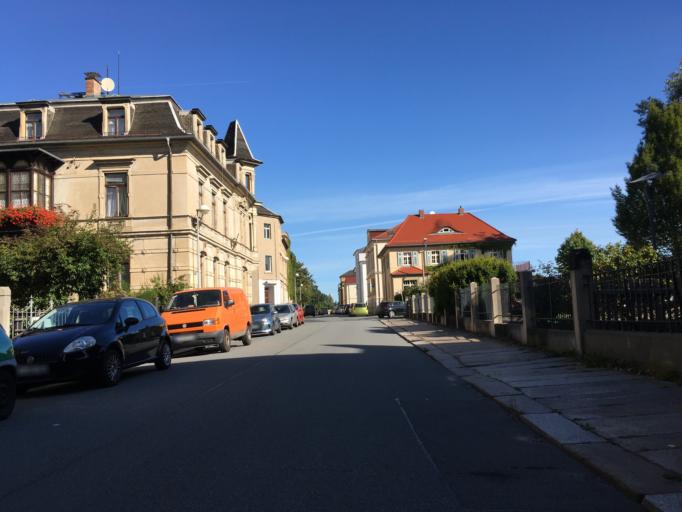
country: DE
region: Saxony
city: Zittau
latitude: 50.9020
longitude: 14.8087
